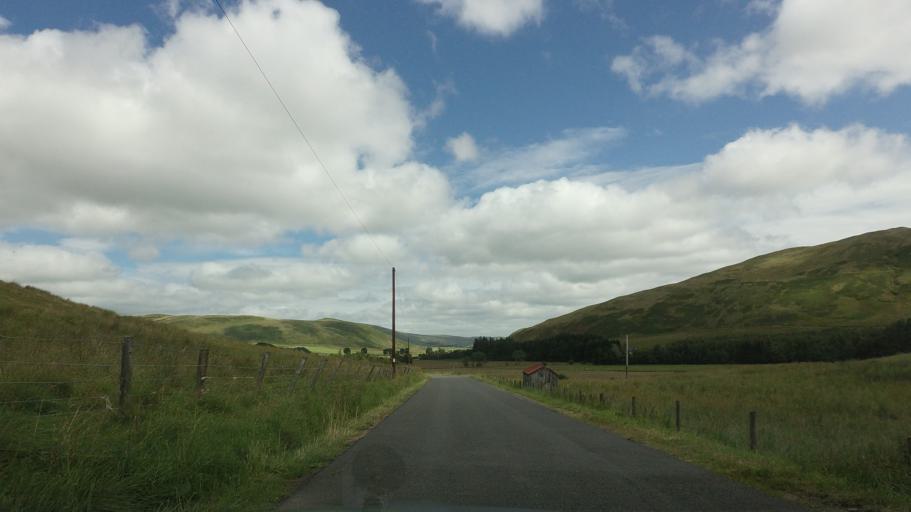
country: GB
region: Scotland
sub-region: The Scottish Borders
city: Innerleithen
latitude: 55.4431
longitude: -3.1052
